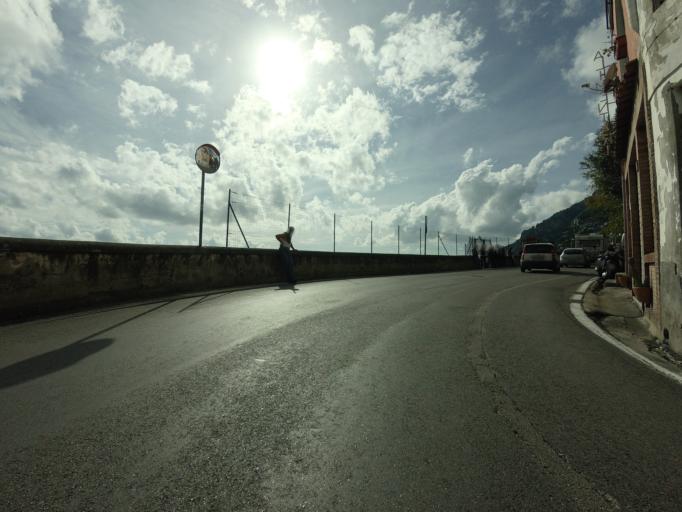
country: IT
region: Campania
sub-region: Provincia di Salerno
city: Positano
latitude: 40.6276
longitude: 14.4915
